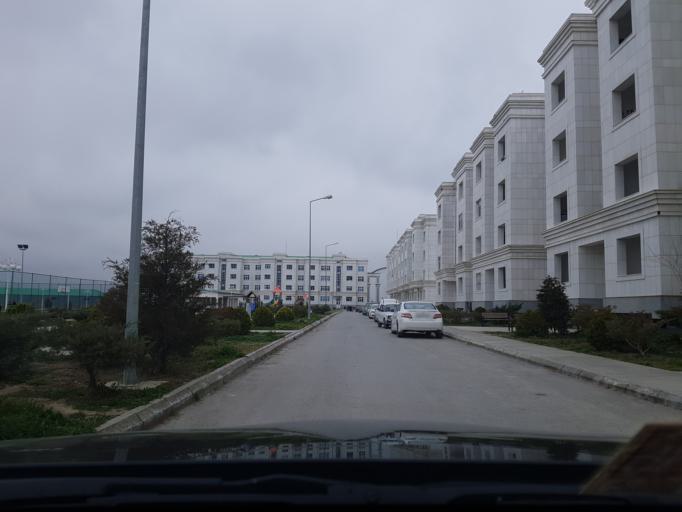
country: TM
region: Ahal
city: Abadan
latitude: 38.1649
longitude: 57.9329
